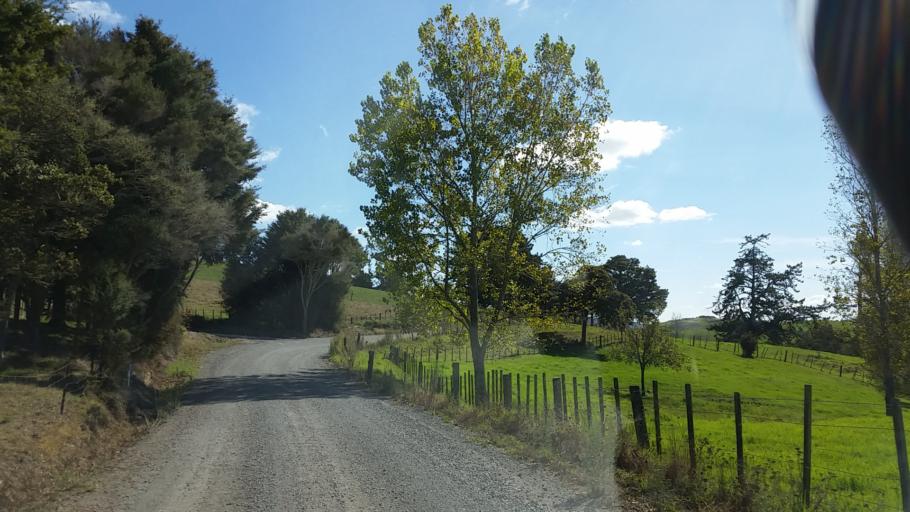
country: NZ
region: Northland
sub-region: Whangarei
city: Maungatapere
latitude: -35.6947
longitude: 174.2295
